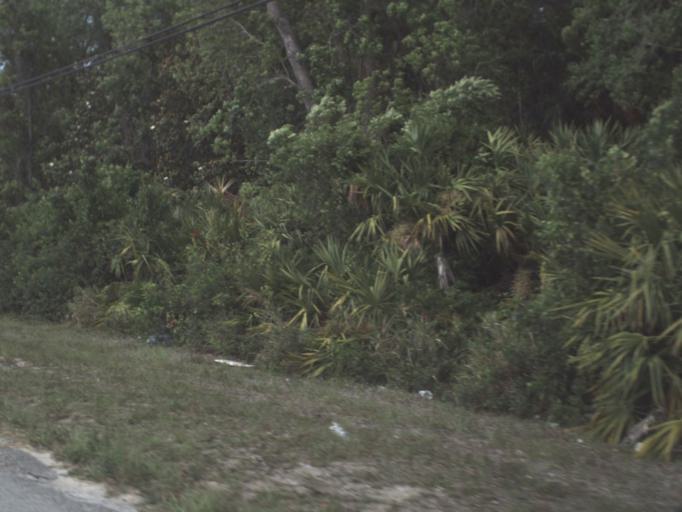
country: US
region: Florida
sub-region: Brevard County
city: Mims
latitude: 28.6485
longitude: -80.8366
